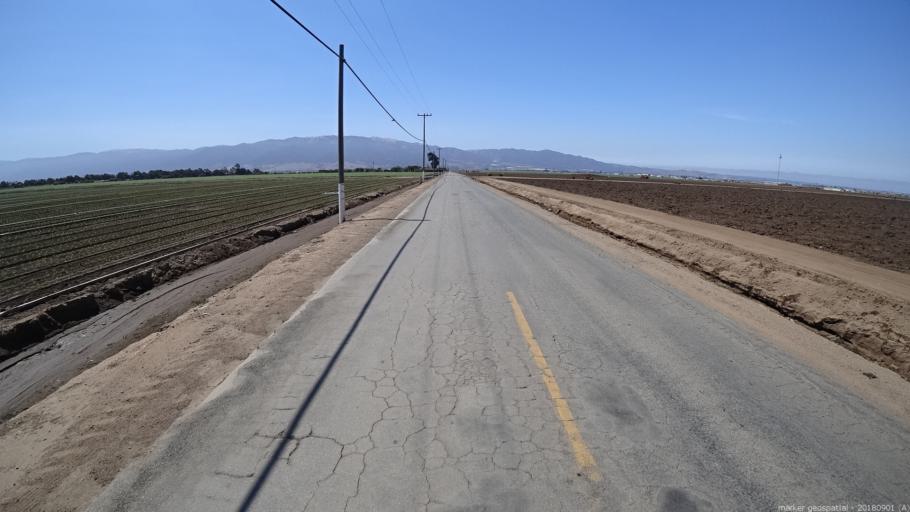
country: US
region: California
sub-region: Monterey County
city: Chualar
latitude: 36.6190
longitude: -121.5372
